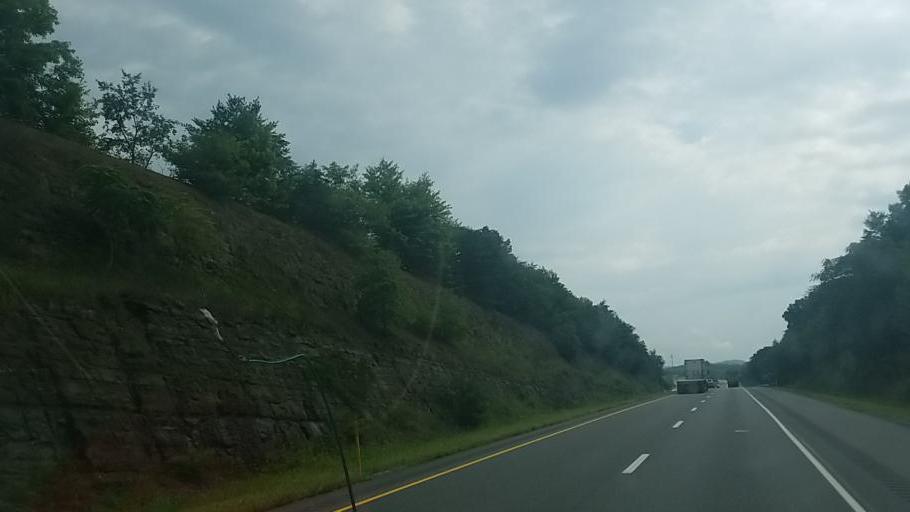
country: US
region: Pennsylvania
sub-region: Juniata County
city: Mifflintown
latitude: 40.5618
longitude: -77.2663
